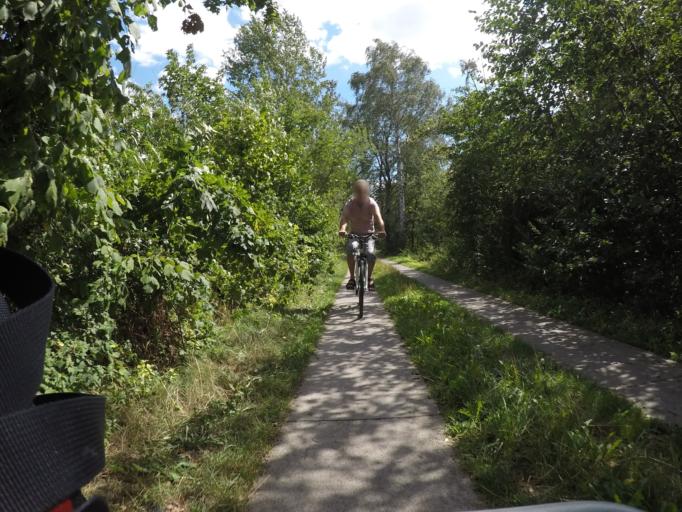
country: DE
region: Lower Saxony
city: Stelle
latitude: 53.4276
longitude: 10.1558
